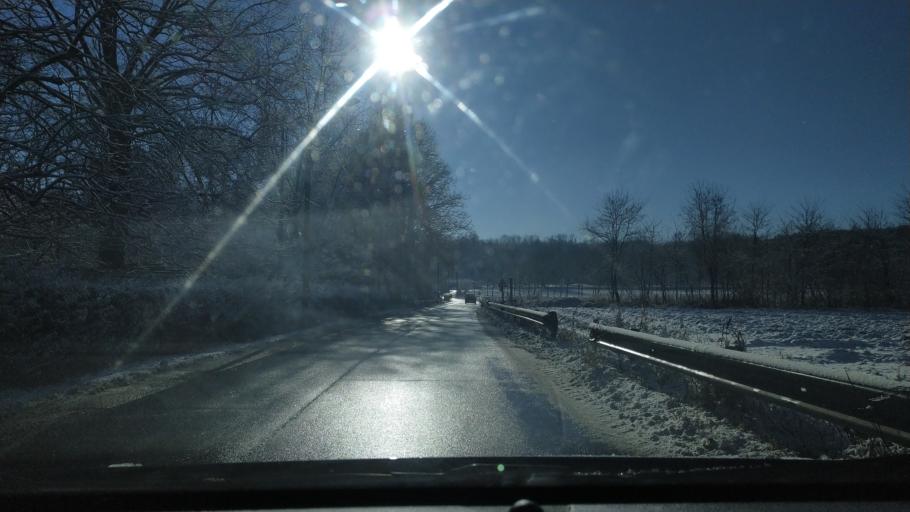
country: IT
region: Piedmont
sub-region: Provincia di Torino
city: Candia Canavese
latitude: 45.3212
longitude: 7.8975
